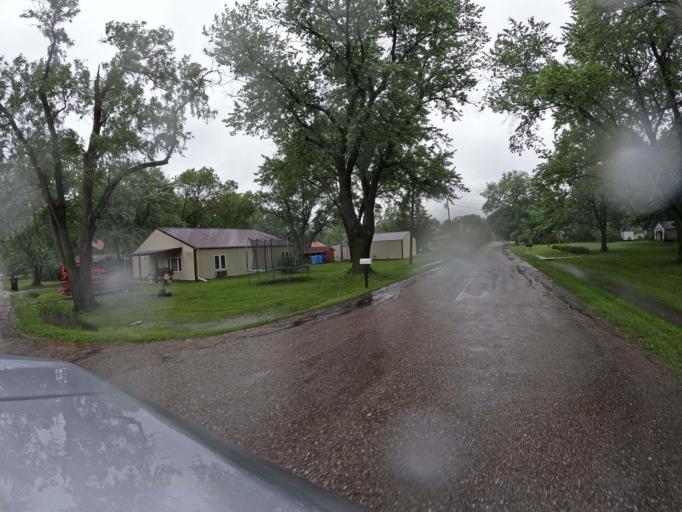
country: US
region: Nebraska
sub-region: Gage County
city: Wymore
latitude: 40.1213
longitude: -96.6753
